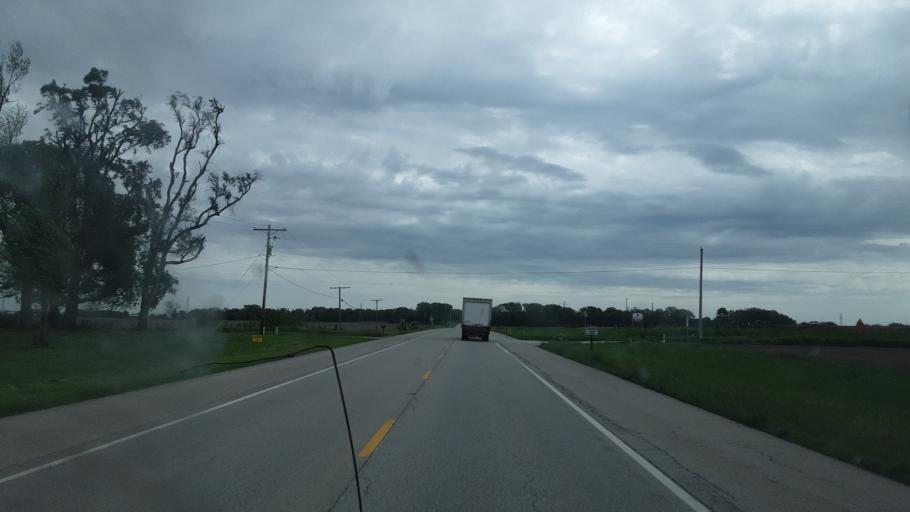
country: US
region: Illinois
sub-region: Tazewell County
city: Delavan
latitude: 40.3053
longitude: -89.6226
